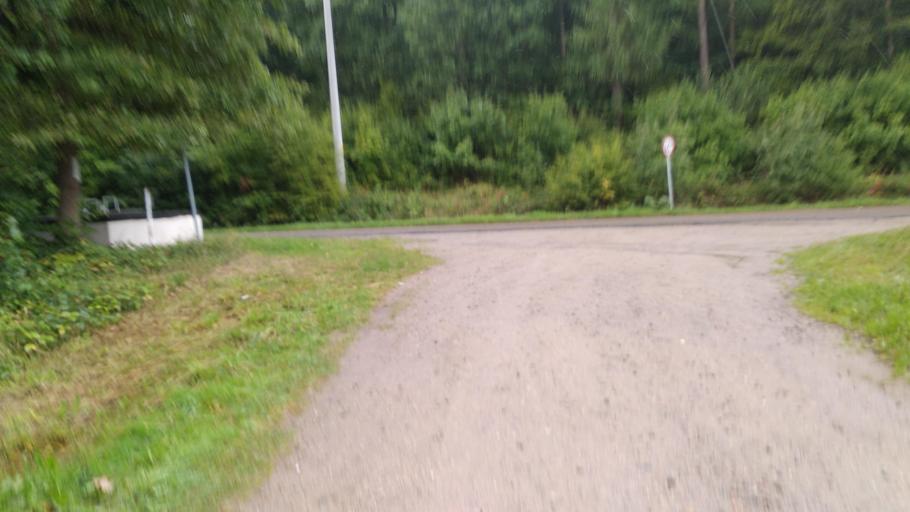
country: PL
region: Pomeranian Voivodeship
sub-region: Powiat wejherowski
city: Goscicino
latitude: 54.6347
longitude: 18.1321
